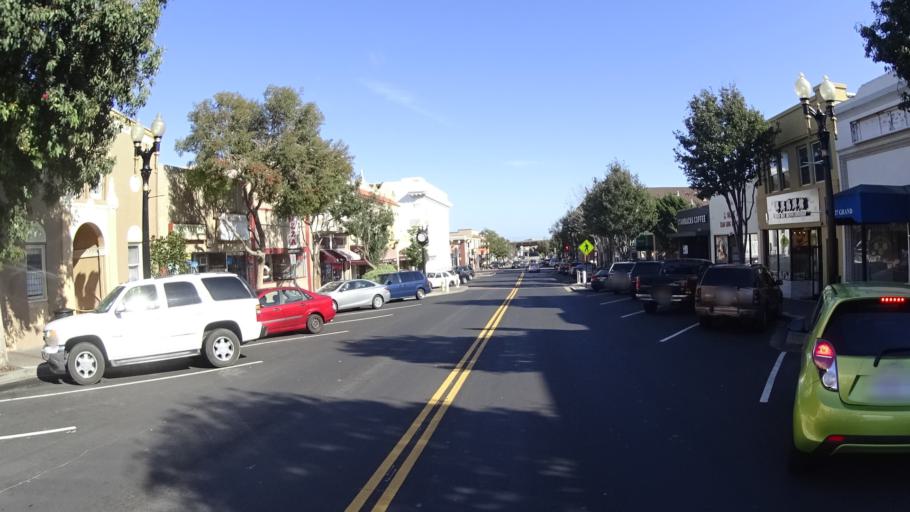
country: US
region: California
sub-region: San Mateo County
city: South San Francisco
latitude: 37.6554
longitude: -122.4113
